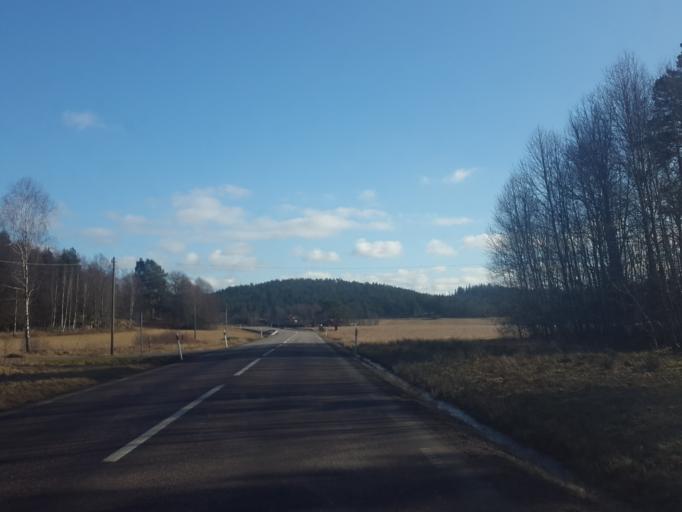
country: SE
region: Vaestra Goetaland
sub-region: Alingsas Kommun
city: Alingsas
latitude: 57.9547
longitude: 12.4597
